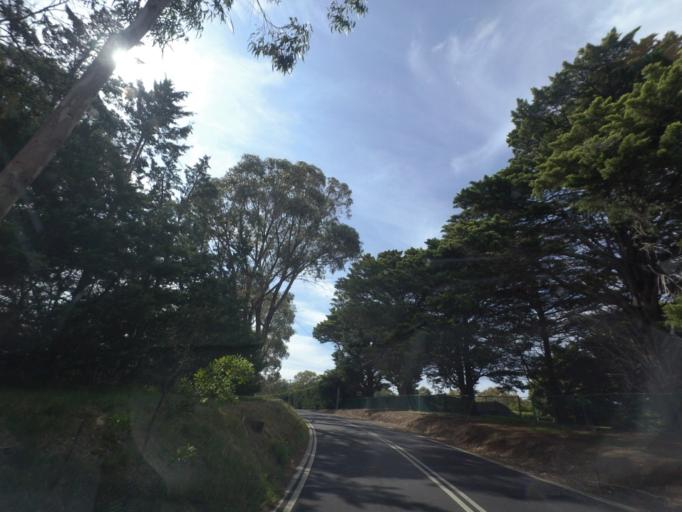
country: AU
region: Victoria
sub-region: Banyule
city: Lower Plenty
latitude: -37.7403
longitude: 145.1062
